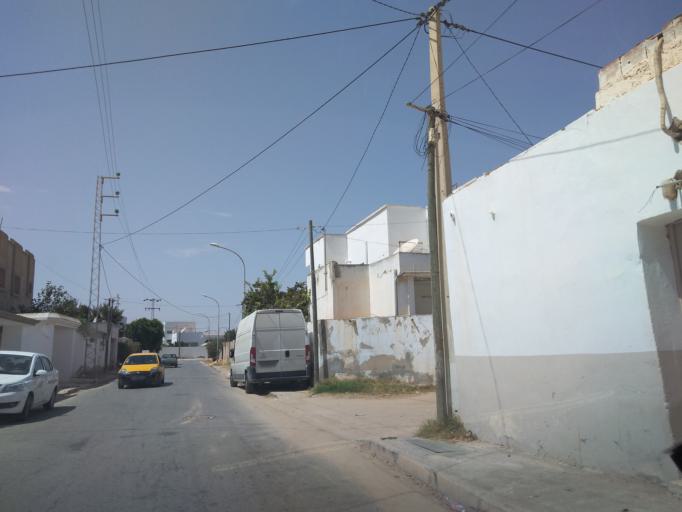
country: TN
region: Safaqis
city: Sfax
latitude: 34.7559
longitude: 10.7404
